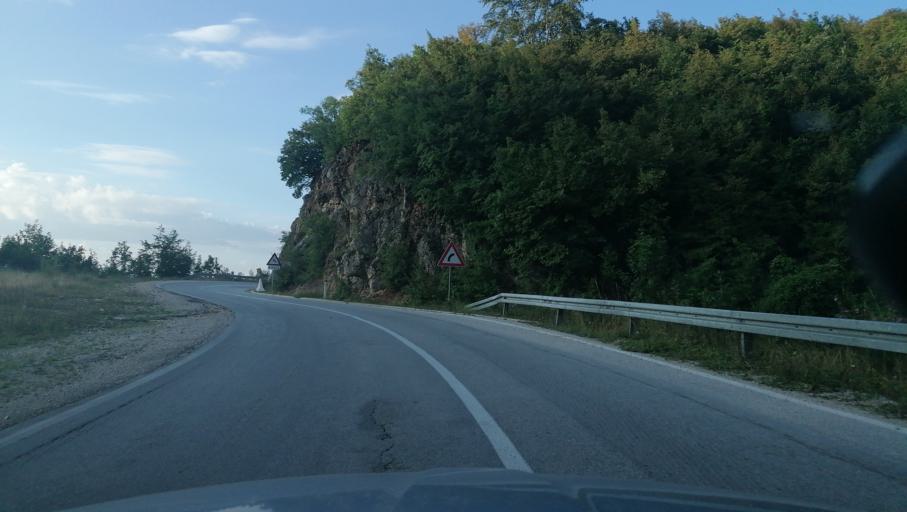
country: BA
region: Federation of Bosnia and Herzegovina
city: Prozor
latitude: 43.8389
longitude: 17.5933
